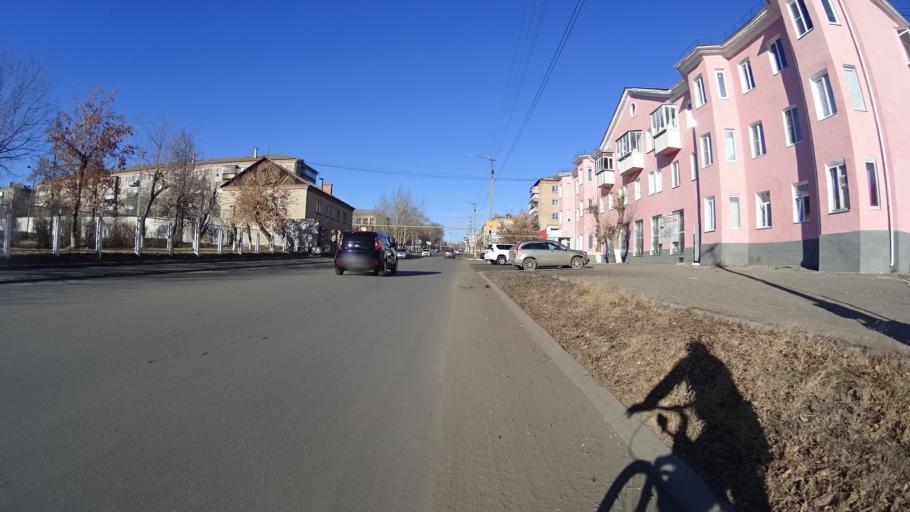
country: RU
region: Chelyabinsk
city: Troitsk
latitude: 54.0782
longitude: 61.5382
